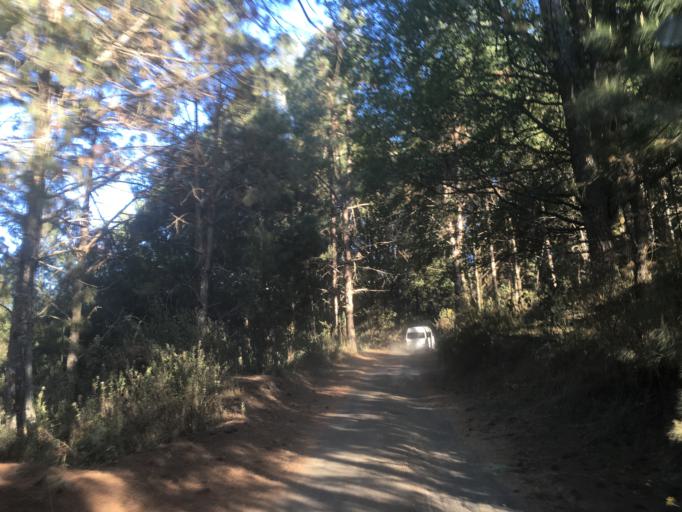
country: MX
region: Michoacan
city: Angahuan
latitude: 19.4784
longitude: -102.2453
